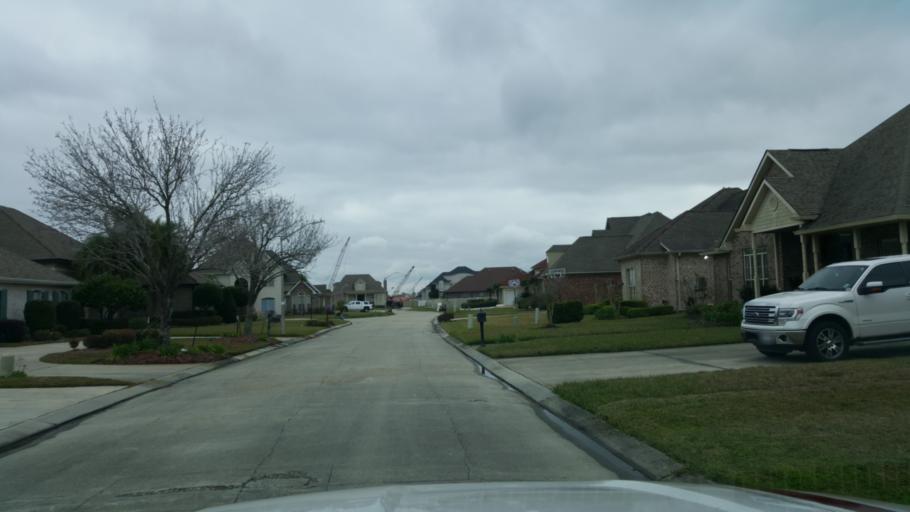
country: US
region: Louisiana
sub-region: Jefferson Parish
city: Woodmere
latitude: 29.8784
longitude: -90.0793
